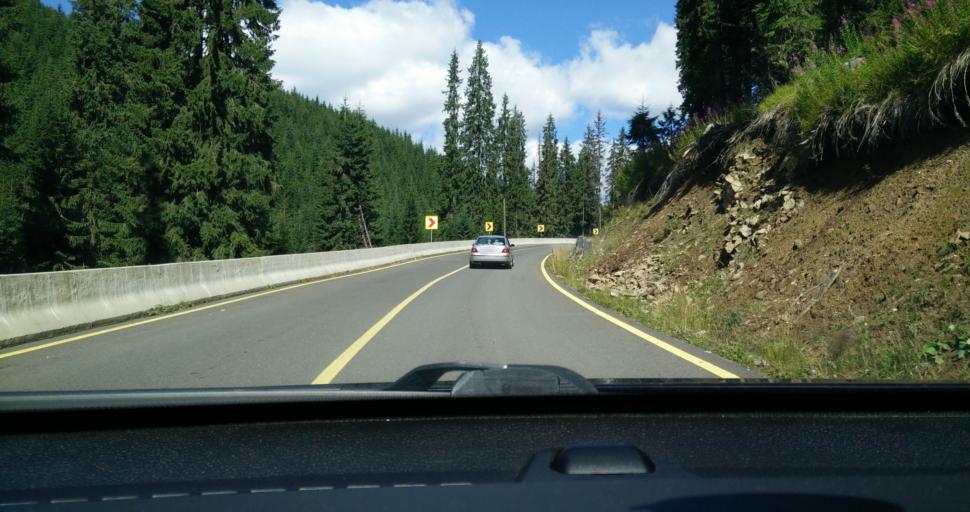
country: RO
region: Hunedoara
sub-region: Oras Petrila
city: Petrila
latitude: 45.4419
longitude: 23.6255
